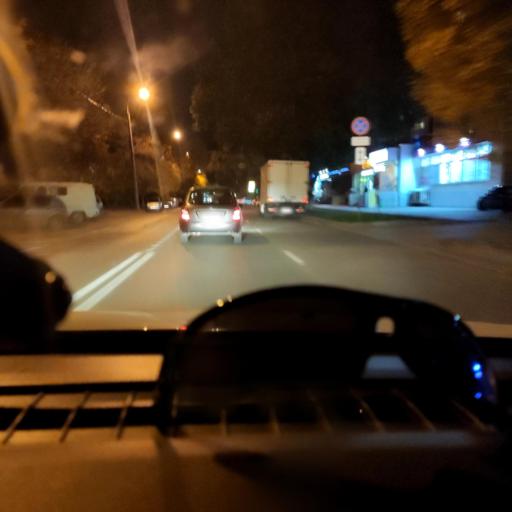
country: RU
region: Samara
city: Samara
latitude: 53.1963
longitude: 50.1667
